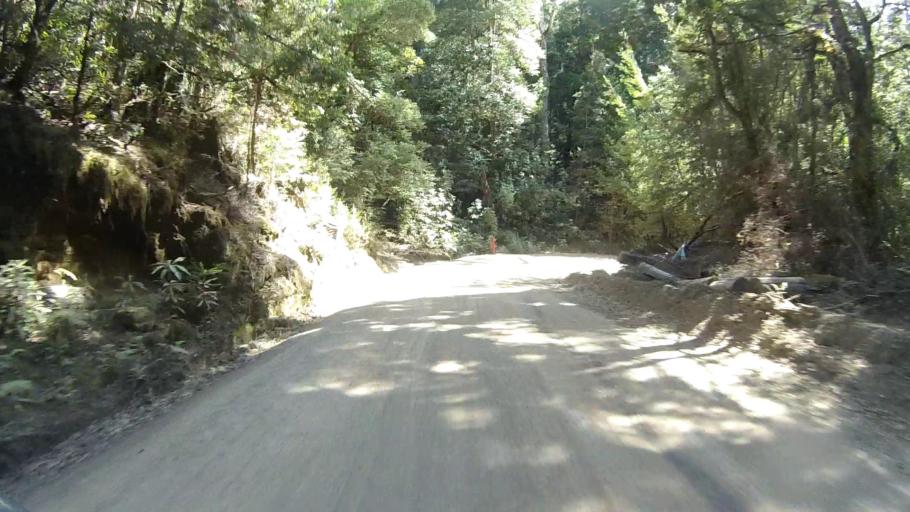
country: AU
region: Tasmania
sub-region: Derwent Valley
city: New Norfolk
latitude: -42.6811
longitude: 146.6753
